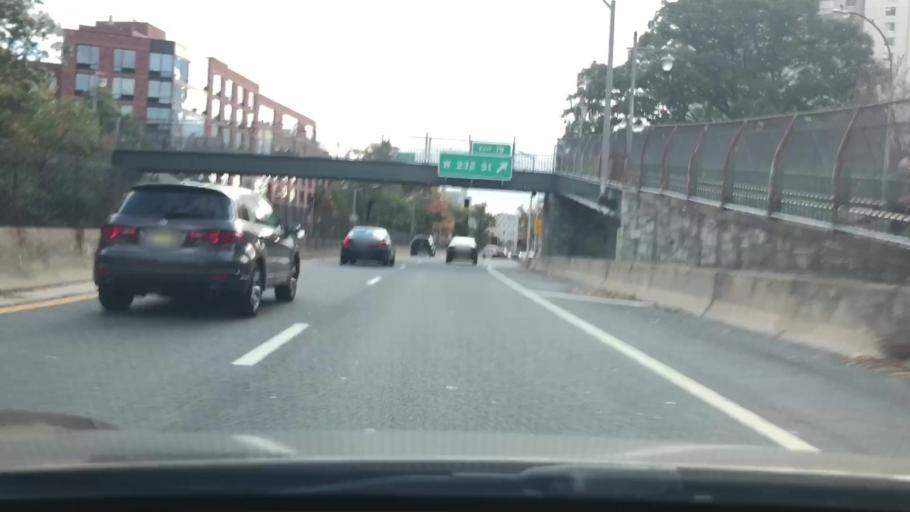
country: US
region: New York
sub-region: New York County
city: Inwood
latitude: 40.8869
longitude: -73.9122
